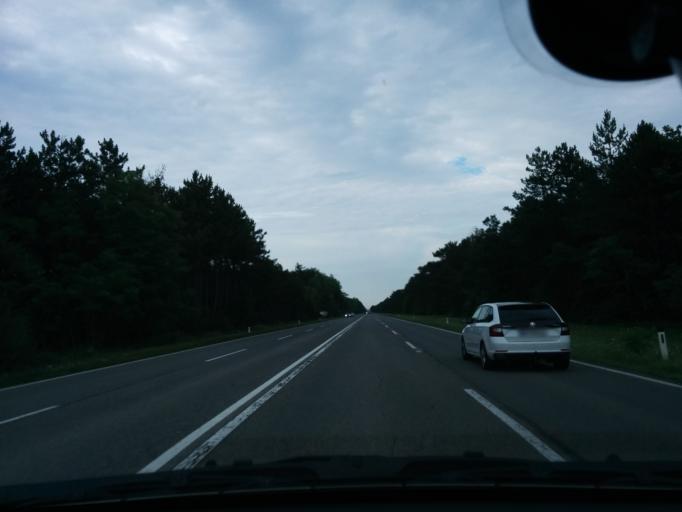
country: AT
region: Lower Austria
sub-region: Politischer Bezirk Neunkirchen
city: Breitenau
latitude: 47.7669
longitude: 16.1651
